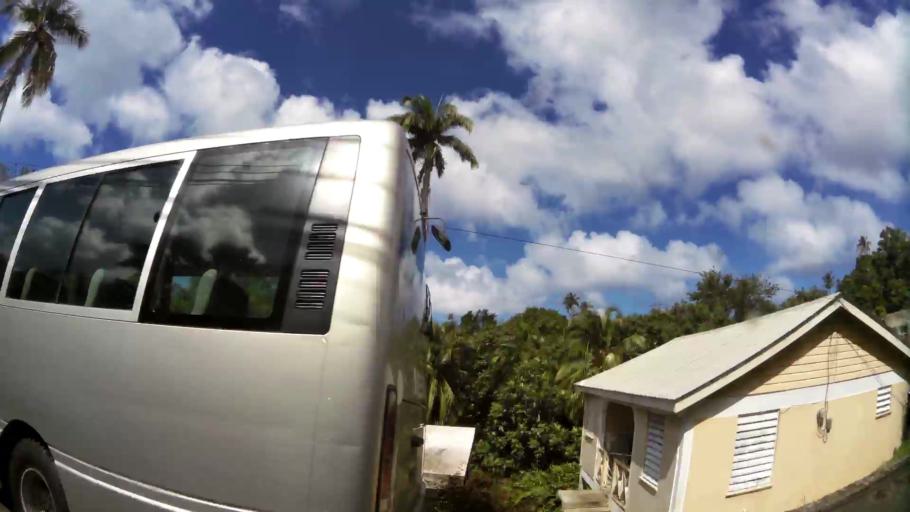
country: DM
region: Saint John
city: Portsmouth
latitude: 15.6148
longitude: -61.4637
